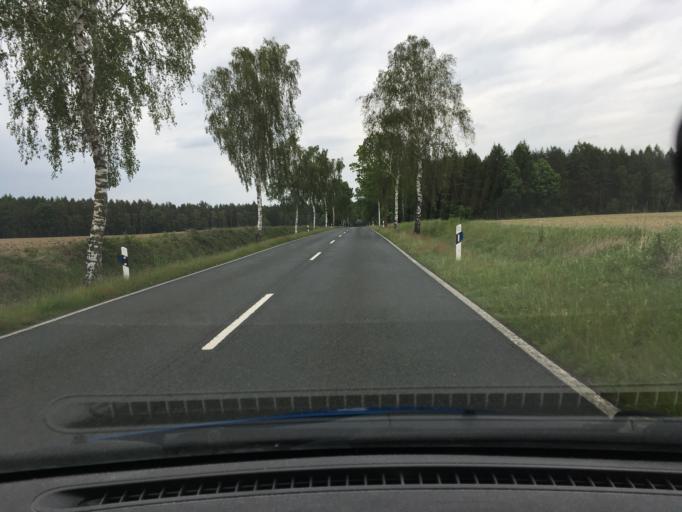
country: DE
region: Lower Saxony
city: Bispingen
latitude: 53.1181
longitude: 10.0378
